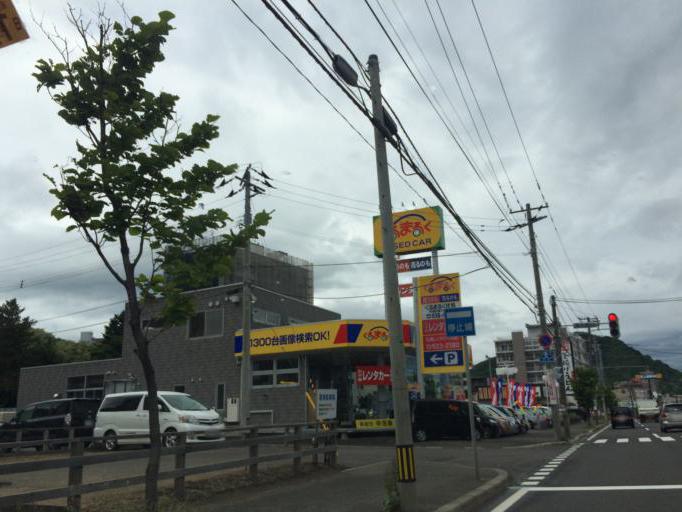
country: JP
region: Hokkaido
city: Sapporo
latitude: 43.0363
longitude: 141.3319
